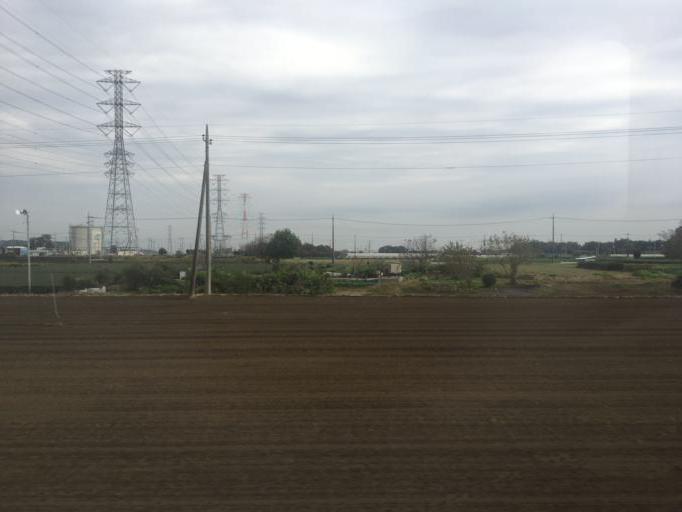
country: JP
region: Saitama
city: Hanno
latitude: 35.8056
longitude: 139.3314
